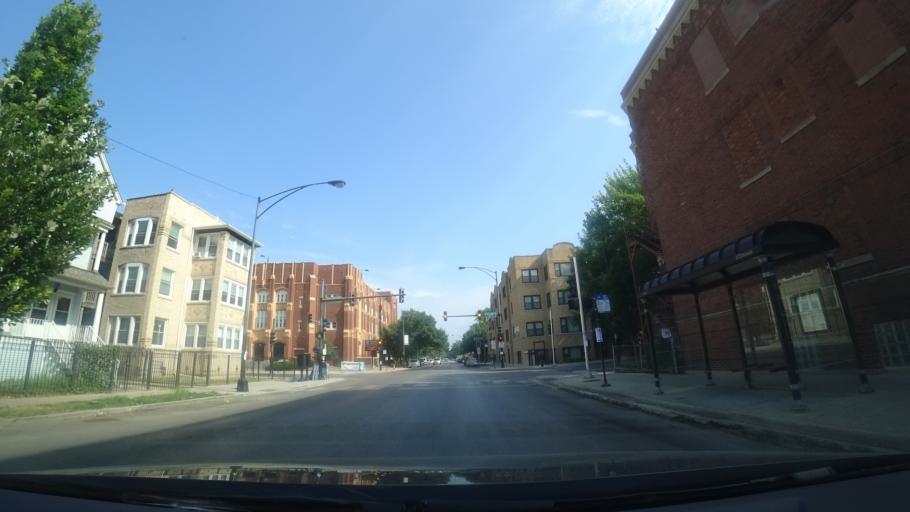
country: US
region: Illinois
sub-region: Cook County
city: Lincolnwood
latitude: 41.9643
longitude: -87.7132
